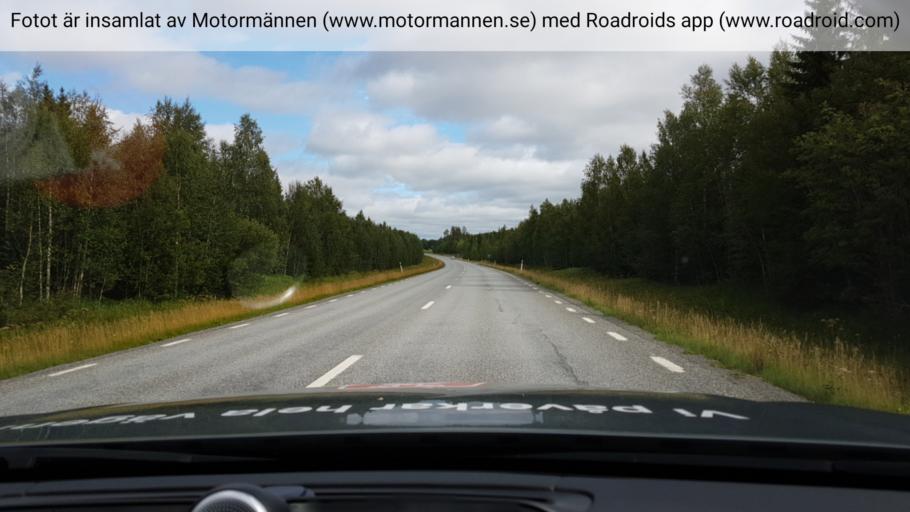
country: SE
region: Jaemtland
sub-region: OEstersunds Kommun
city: Lit
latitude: 63.4265
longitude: 15.1160
